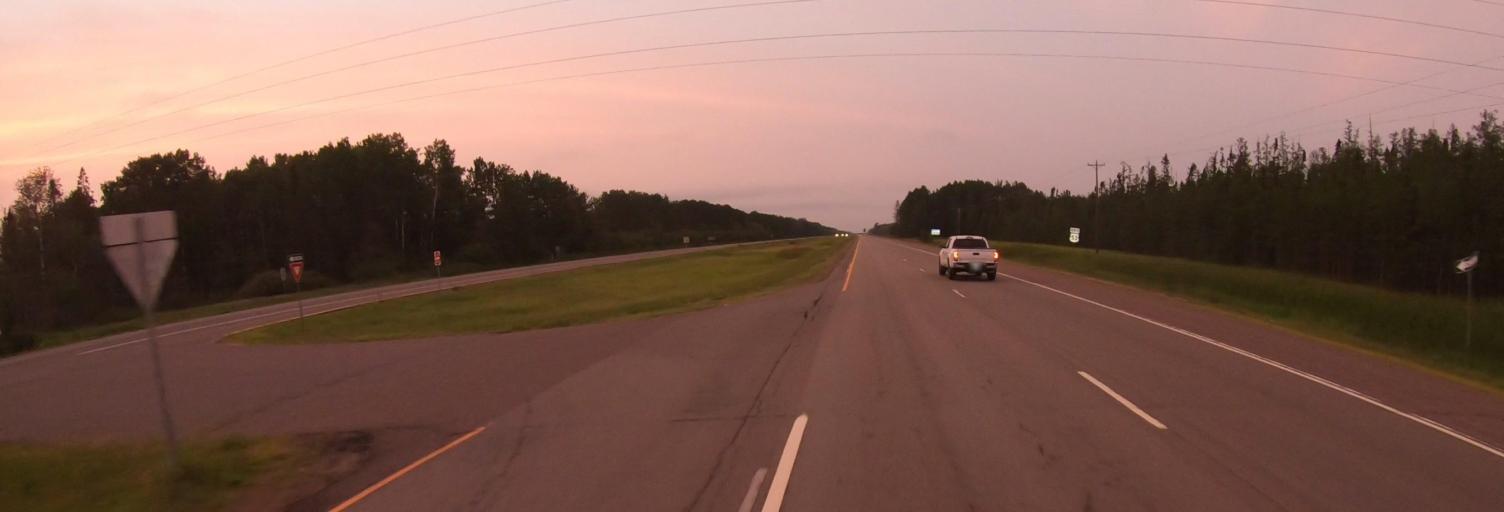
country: US
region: Minnesota
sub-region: Saint Louis County
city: Hermantown
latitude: 47.0866
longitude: -92.4715
